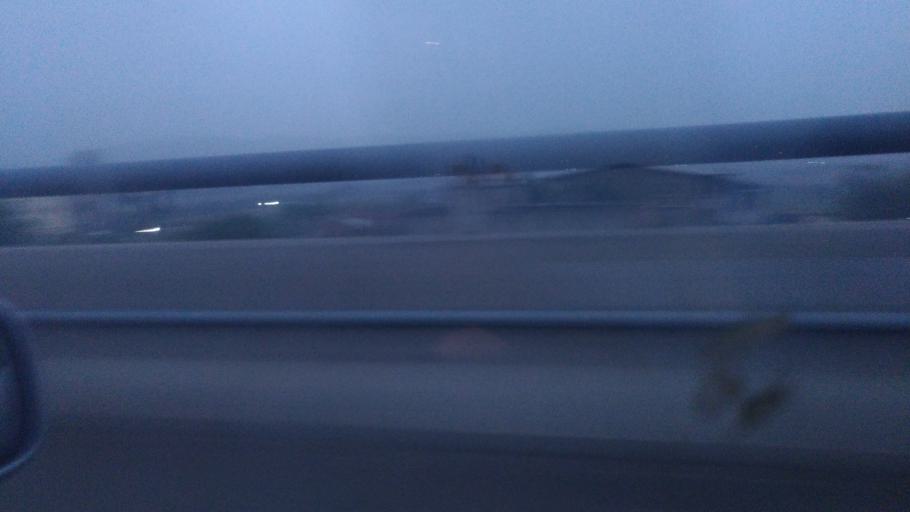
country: TW
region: Taiwan
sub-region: Miaoli
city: Miaoli
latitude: 24.4650
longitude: 120.6563
